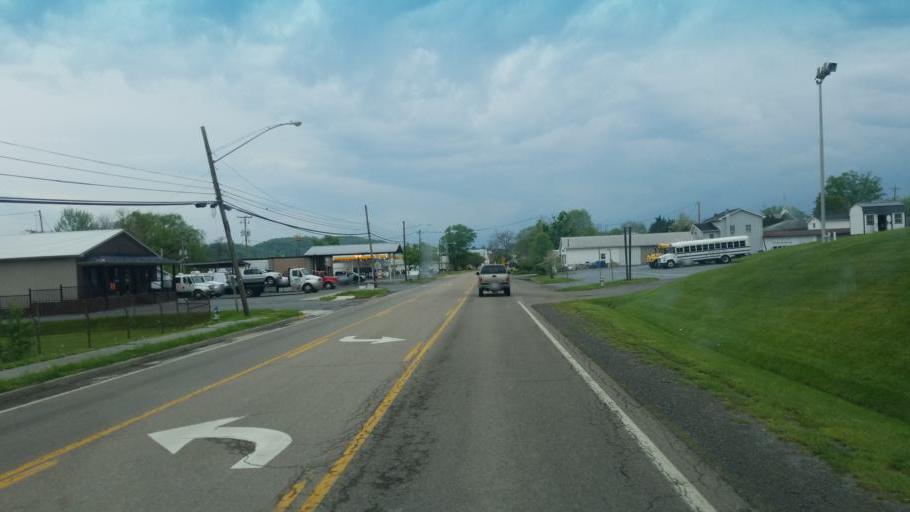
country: US
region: Virginia
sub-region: Smyth County
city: Chilhowie
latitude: 36.8019
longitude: -81.6775
